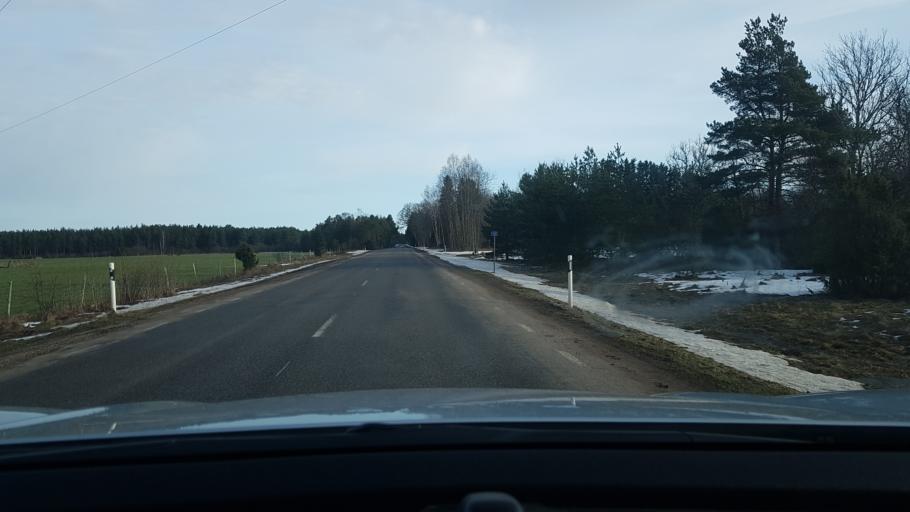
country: EE
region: Saare
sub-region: Kuressaare linn
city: Kuressaare
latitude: 58.3817
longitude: 22.6331
